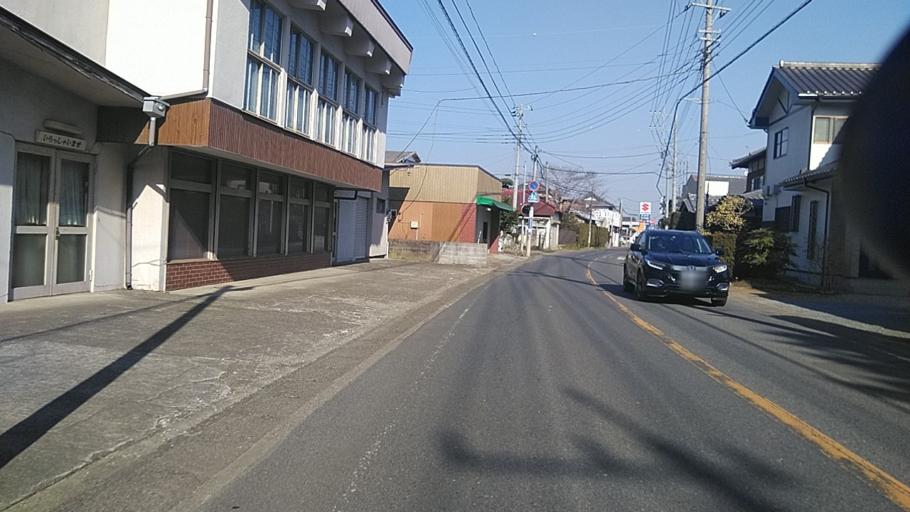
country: JP
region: Chiba
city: Yokaichiba
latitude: 35.6949
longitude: 140.5342
